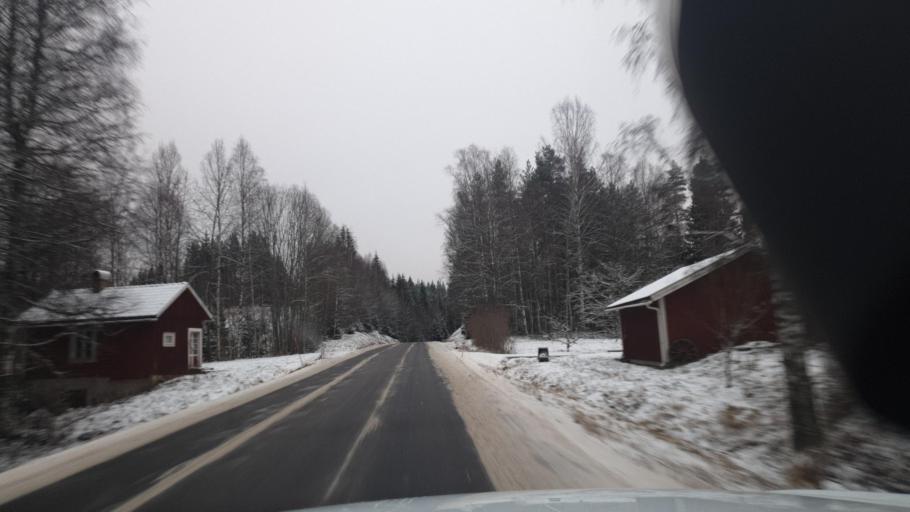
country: SE
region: Vaermland
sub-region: Arvika Kommun
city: Arvika
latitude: 59.9031
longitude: 12.6428
